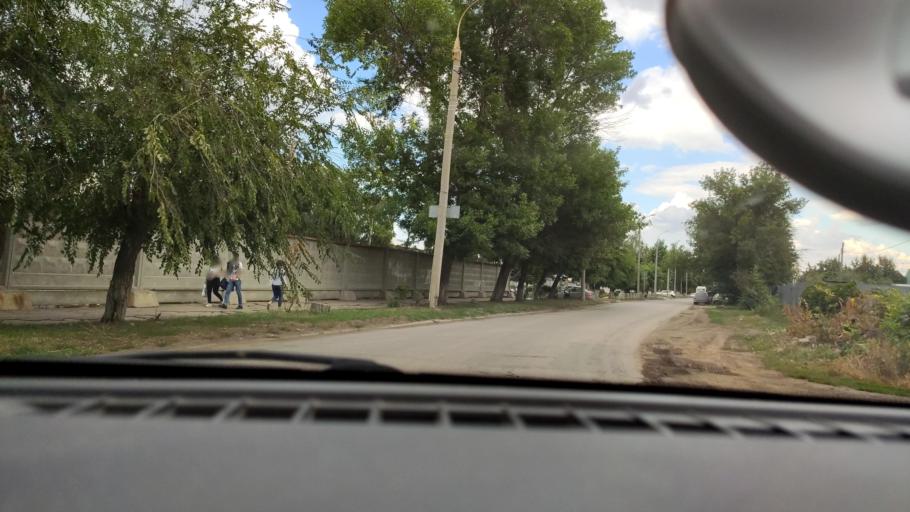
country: RU
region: Samara
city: Novokuybyshevsk
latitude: 53.1037
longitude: 50.0371
